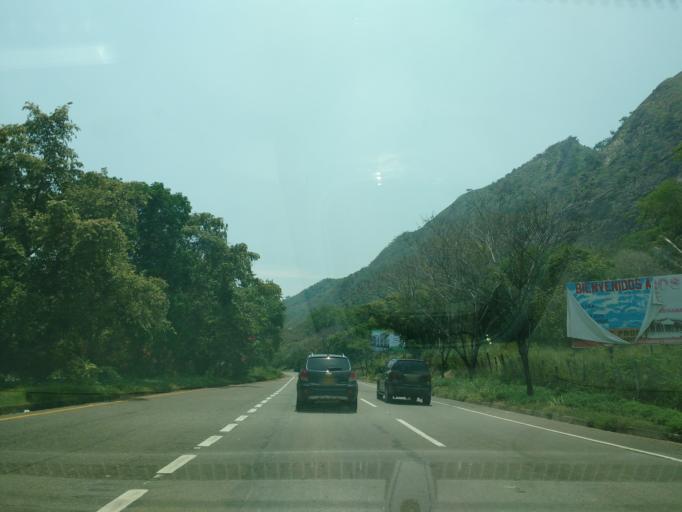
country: CO
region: Cundinamarca
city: Ricaurte
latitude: 4.2499
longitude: -74.7286
